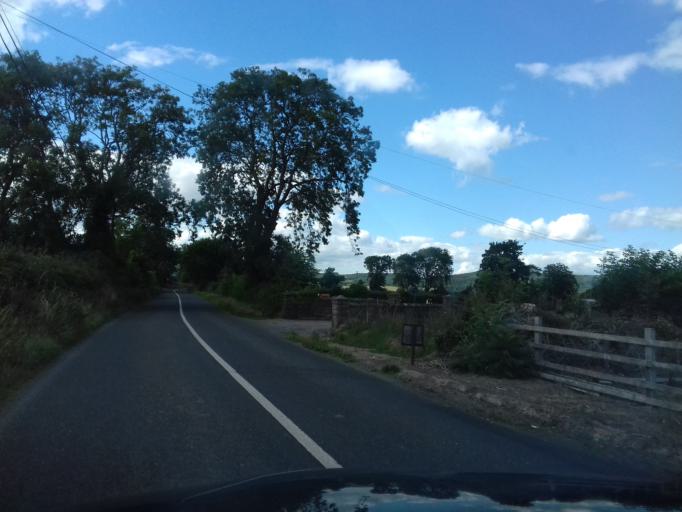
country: IE
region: Munster
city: Carrick-on-Suir
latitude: 52.3659
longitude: -7.4393
